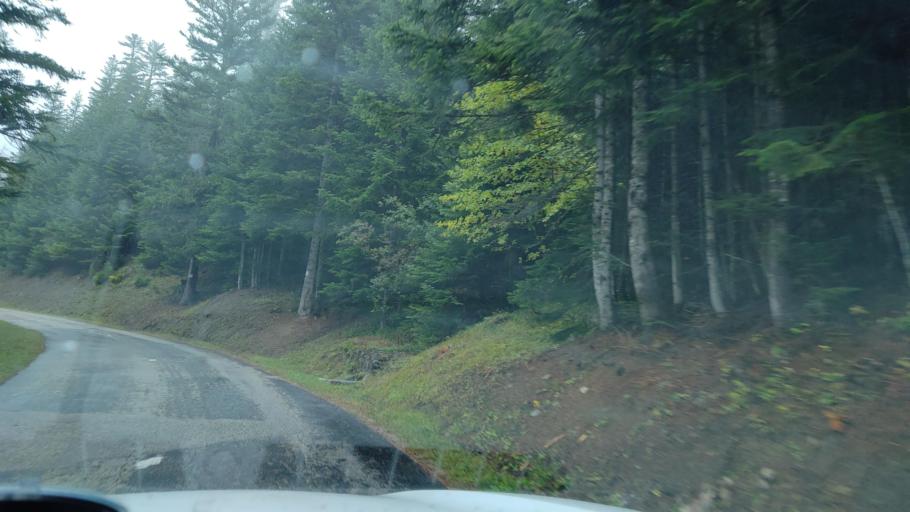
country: FR
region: Rhone-Alpes
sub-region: Departement de la Savoie
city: Modane
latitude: 45.2983
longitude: 6.8214
